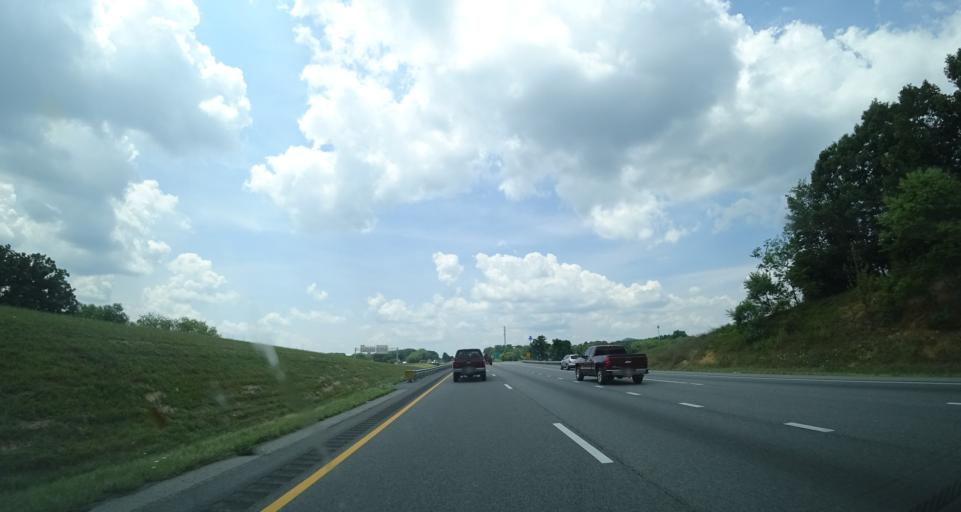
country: US
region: Virginia
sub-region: Wythe County
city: Wytheville
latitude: 36.9595
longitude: -81.0606
